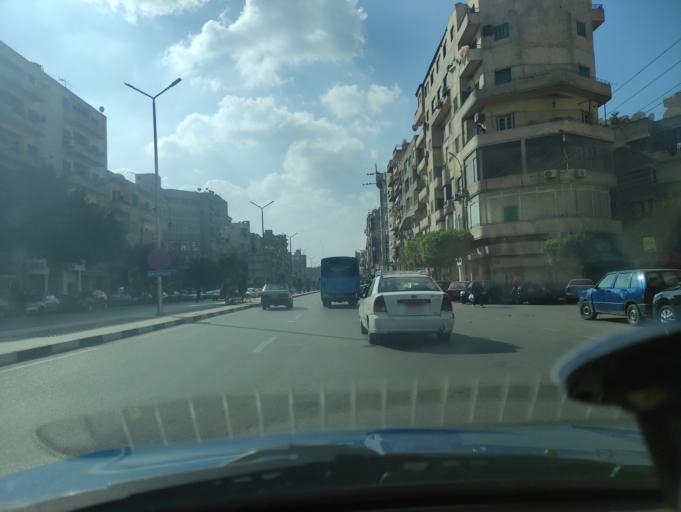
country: EG
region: Muhafazat al Qahirah
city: Cairo
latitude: 30.1000
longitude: 31.3422
